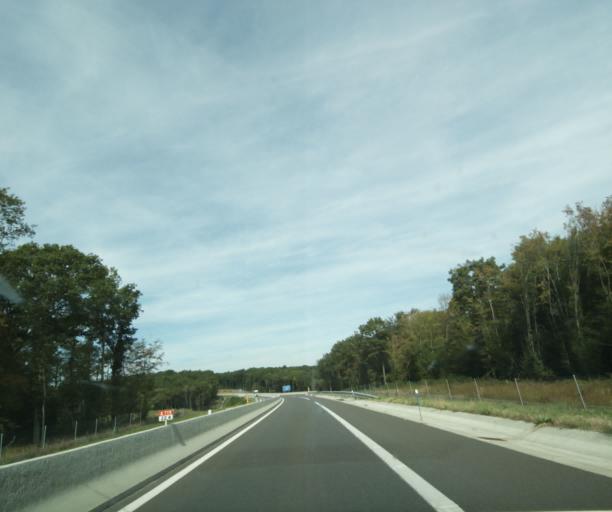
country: FR
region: Auvergne
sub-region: Departement de l'Allier
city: Vendat
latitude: 46.1286
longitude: 3.3627
